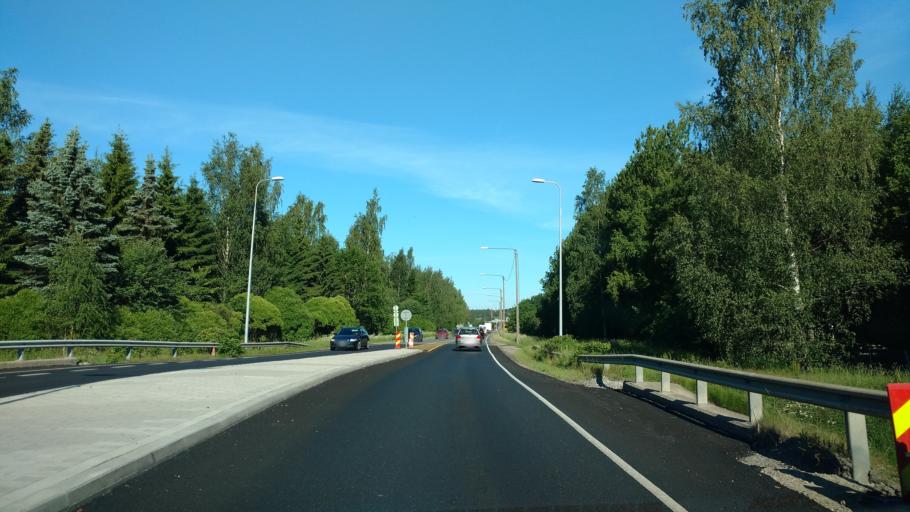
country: FI
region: Varsinais-Suomi
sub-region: Salo
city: Salo
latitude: 60.3914
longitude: 23.1432
